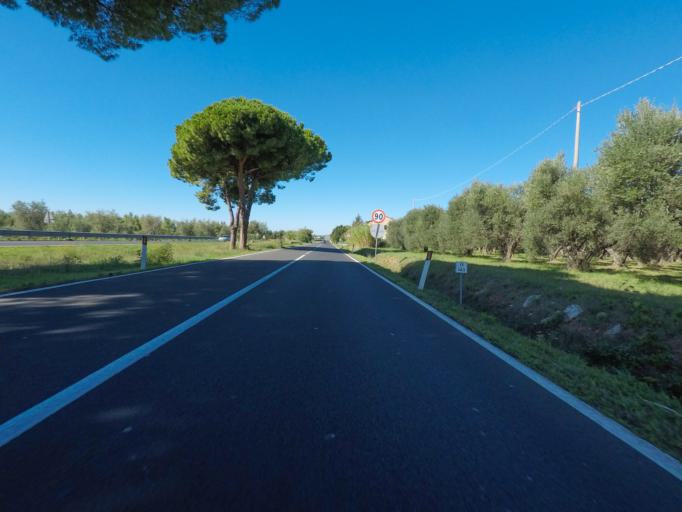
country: IT
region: Tuscany
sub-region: Provincia di Grosseto
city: Orbetello Scalo
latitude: 42.4554
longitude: 11.2507
